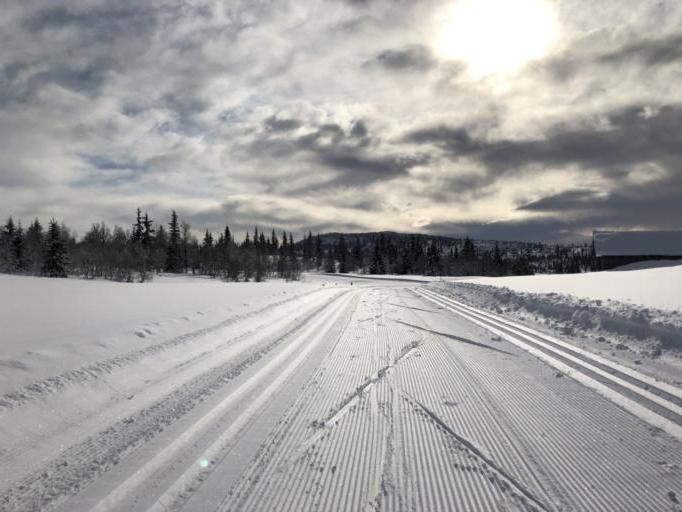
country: NO
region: Oppland
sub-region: Gausdal
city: Segalstad bru
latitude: 61.3168
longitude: 10.0606
